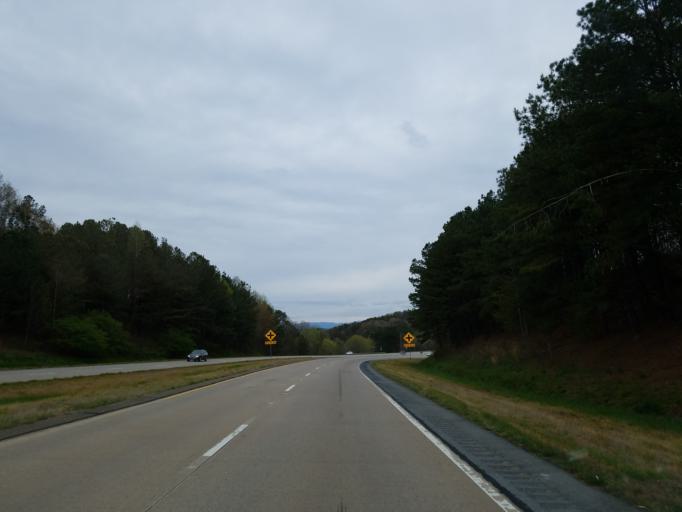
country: US
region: Georgia
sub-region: Pickens County
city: Jasper
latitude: 34.5636
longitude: -84.5219
